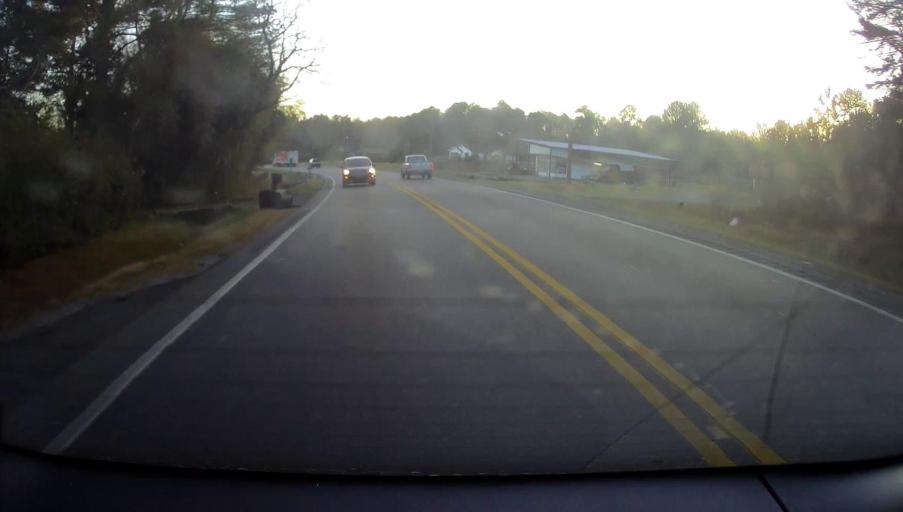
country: US
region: Alabama
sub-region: Etowah County
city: Attalla
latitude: 34.0287
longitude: -86.1193
